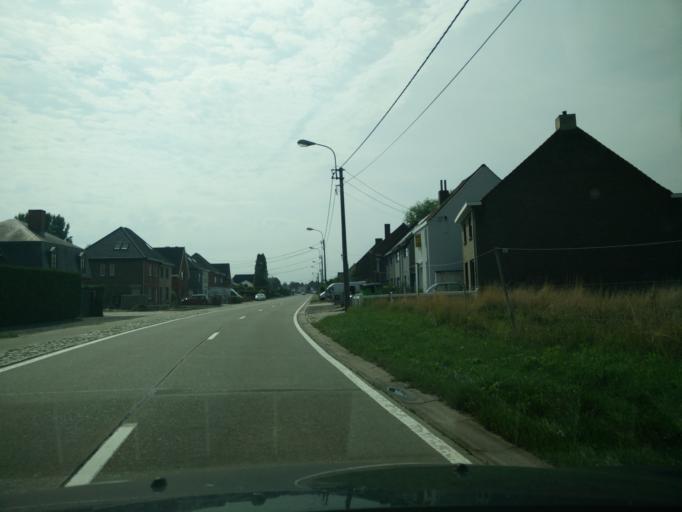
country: BE
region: Flanders
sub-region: Provincie Oost-Vlaanderen
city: Merelbeke
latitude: 50.9757
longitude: 3.7396
